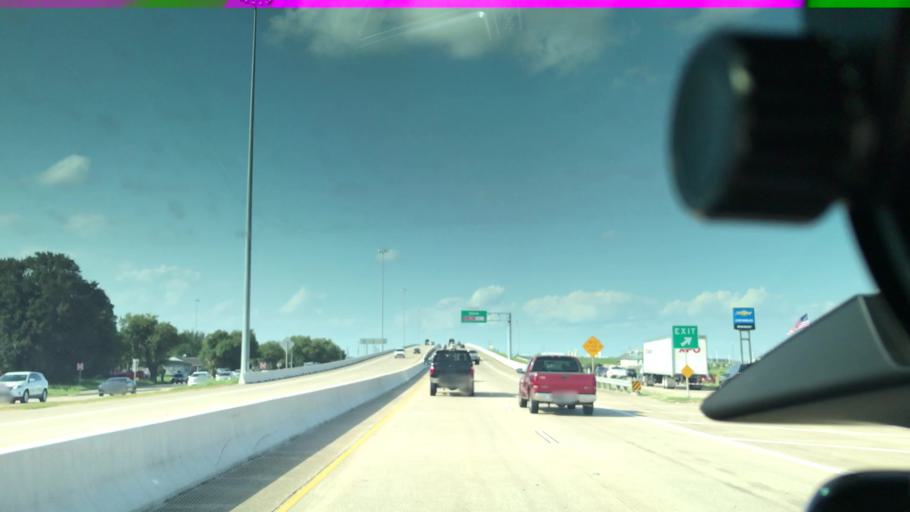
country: US
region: Texas
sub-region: Harris County
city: Deer Park
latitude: 29.7063
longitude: -95.1534
